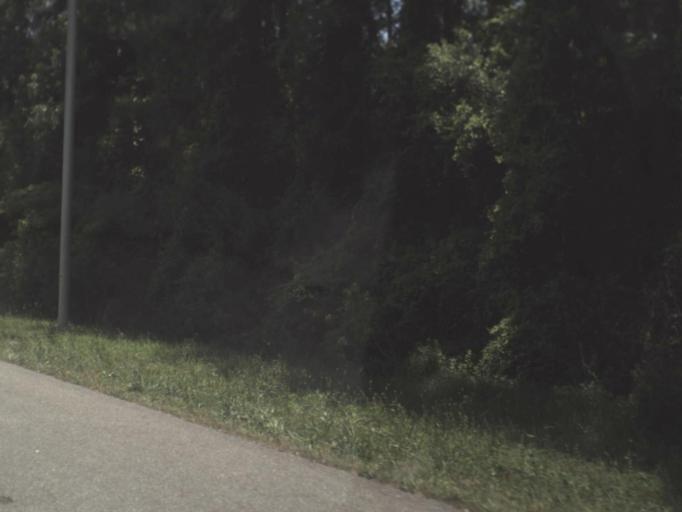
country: US
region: Florida
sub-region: Clay County
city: Bellair-Meadowbrook Terrace
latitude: 30.2801
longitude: -81.7713
